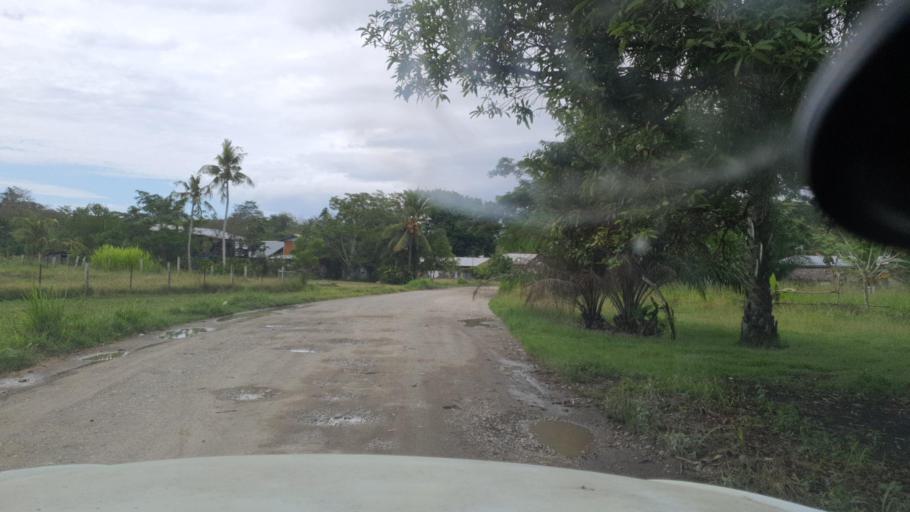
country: SB
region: Guadalcanal
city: Honiara
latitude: -9.4468
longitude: 160.0738
